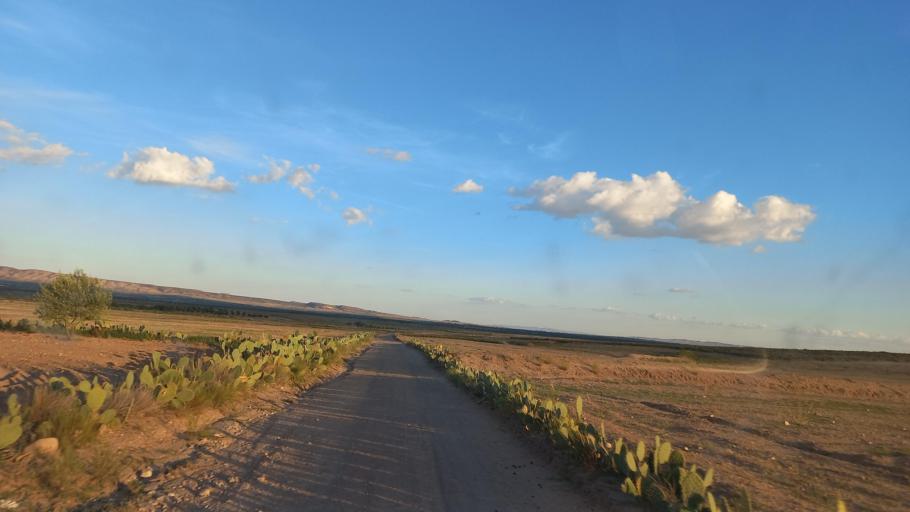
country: TN
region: Al Qasrayn
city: Sbiba
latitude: 35.3513
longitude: 9.0208
